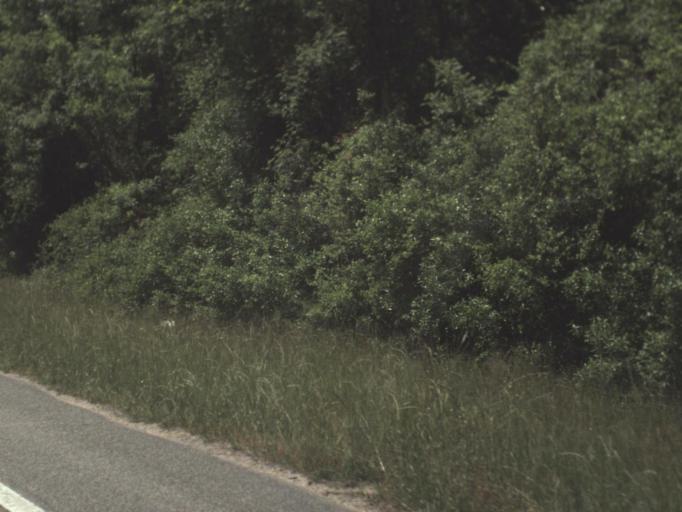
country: US
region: Florida
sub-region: Jackson County
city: Marianna
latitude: 30.6186
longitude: -85.1807
